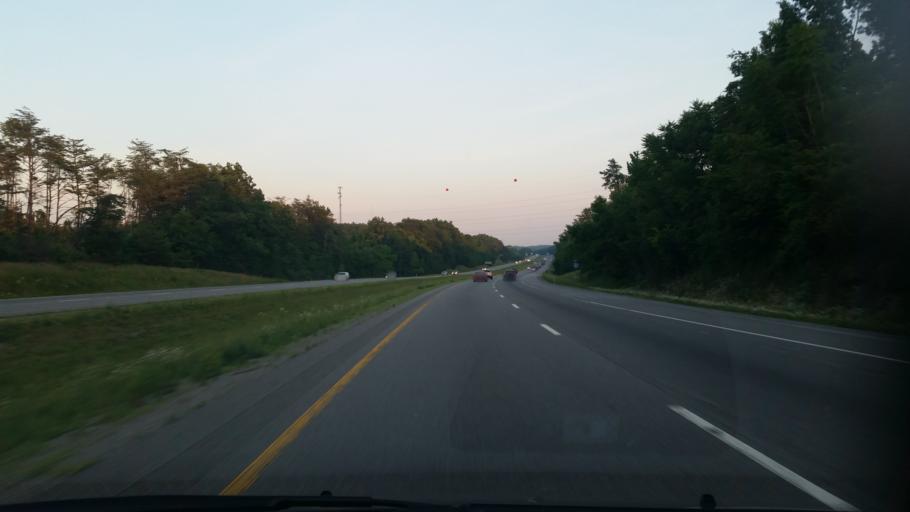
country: US
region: Tennessee
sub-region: Putnam County
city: Monterey
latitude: 36.1358
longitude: -85.2632
